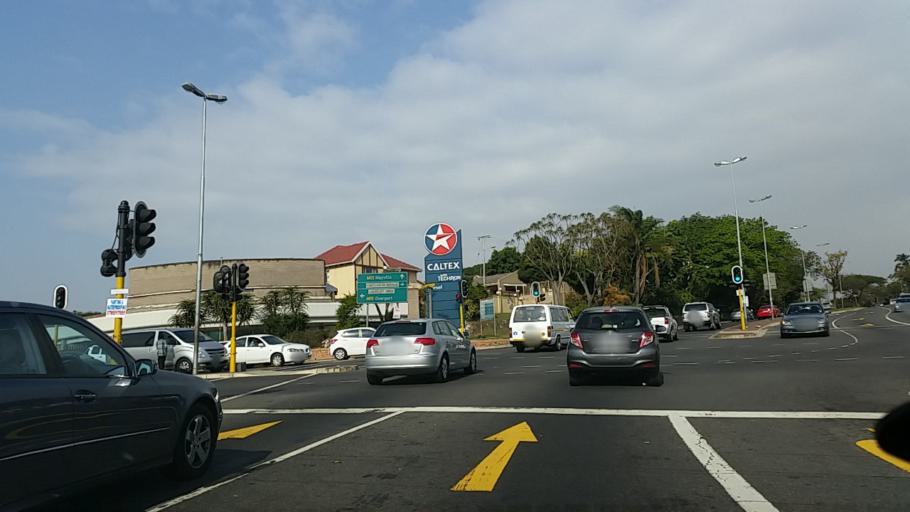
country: ZA
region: KwaZulu-Natal
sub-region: eThekwini Metropolitan Municipality
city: Berea
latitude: -29.8325
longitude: 30.9687
